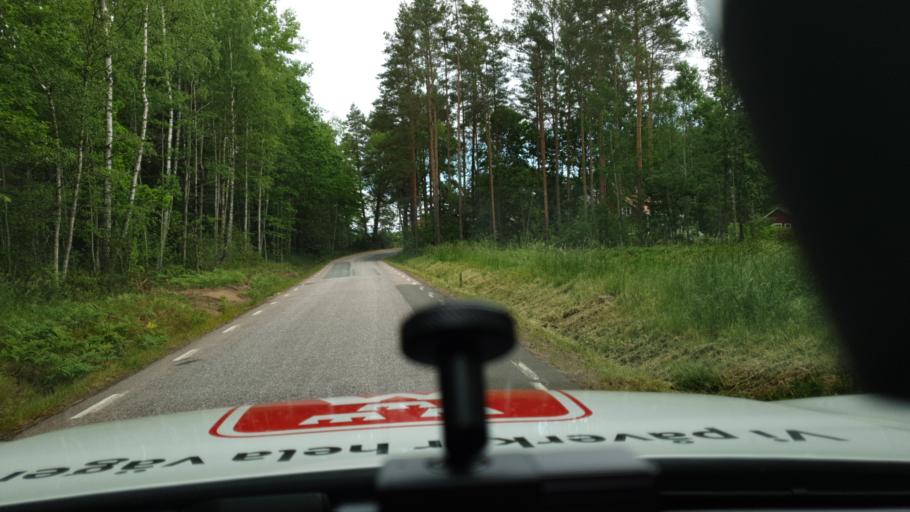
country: SE
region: Vaestra Goetaland
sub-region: Karlsborgs Kommun
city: Molltorp
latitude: 58.4334
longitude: 14.3896
